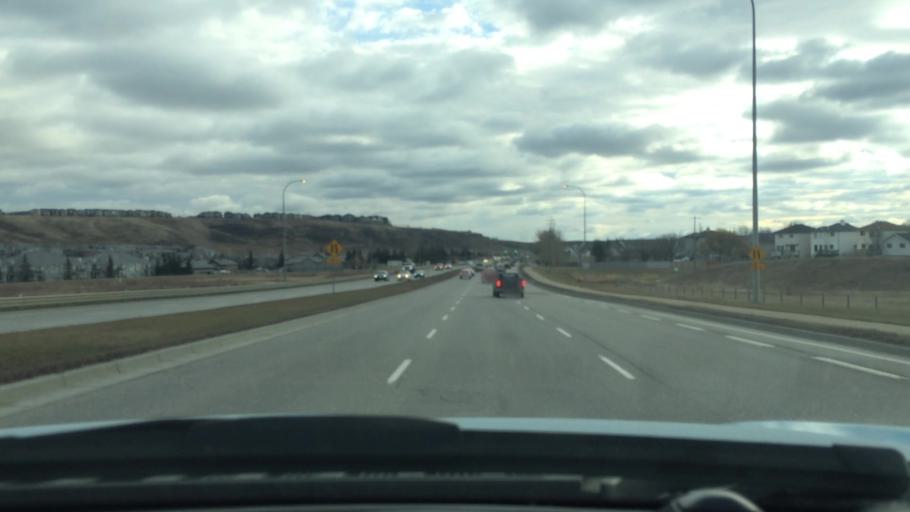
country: CA
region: Alberta
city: Calgary
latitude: 51.1553
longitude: -114.1115
